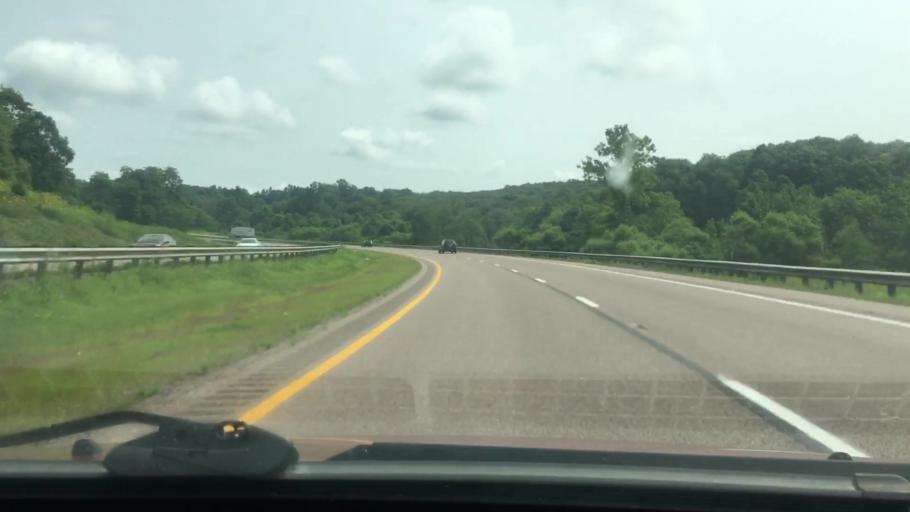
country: US
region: Maryland
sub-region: Garrett County
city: Oakland
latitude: 39.6972
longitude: -79.3236
